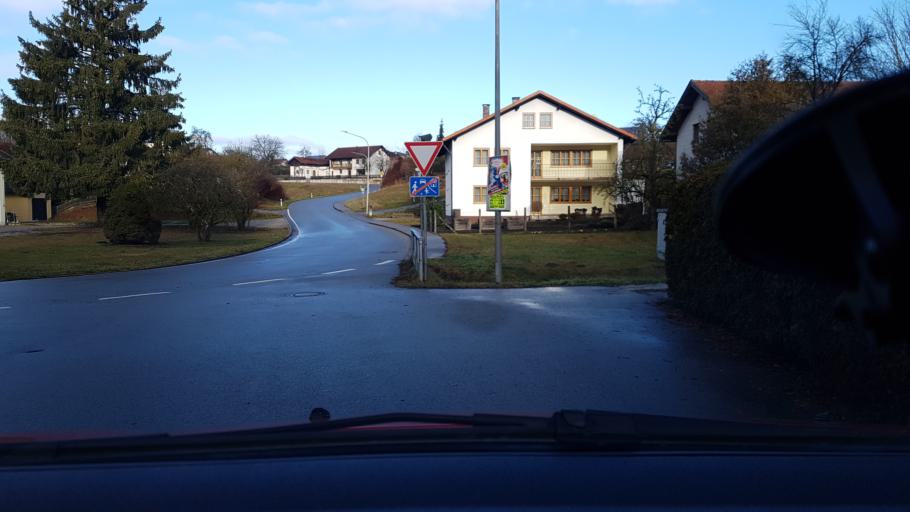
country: DE
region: Bavaria
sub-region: Lower Bavaria
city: Stubenberg
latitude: 48.3091
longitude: 13.0744
